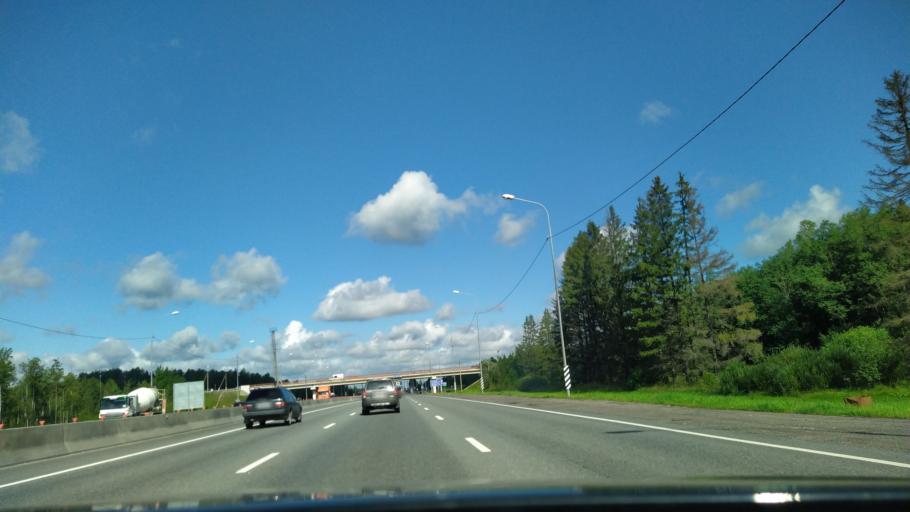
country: RU
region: Leningrad
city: Ul'yanovka
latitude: 59.6040
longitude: 30.7623
